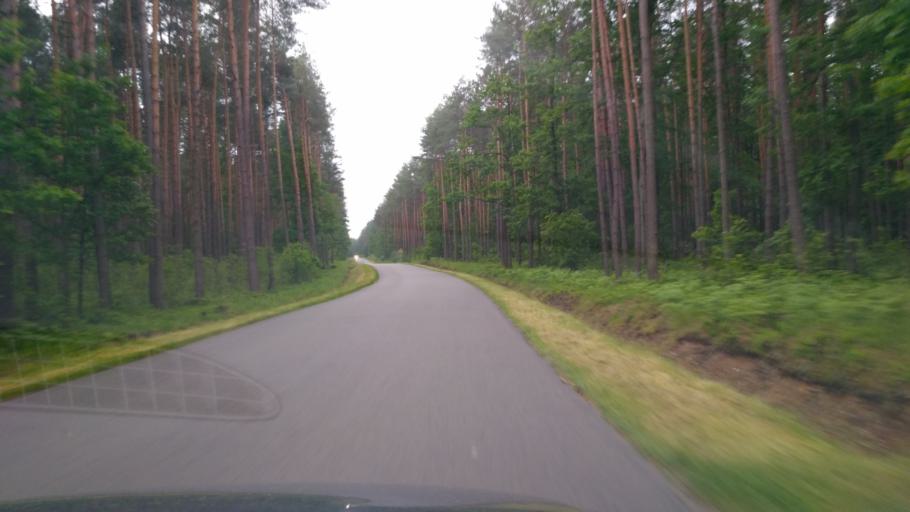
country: PL
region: Subcarpathian Voivodeship
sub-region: Powiat kolbuszowski
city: Niwiska
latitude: 50.1973
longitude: 21.6562
